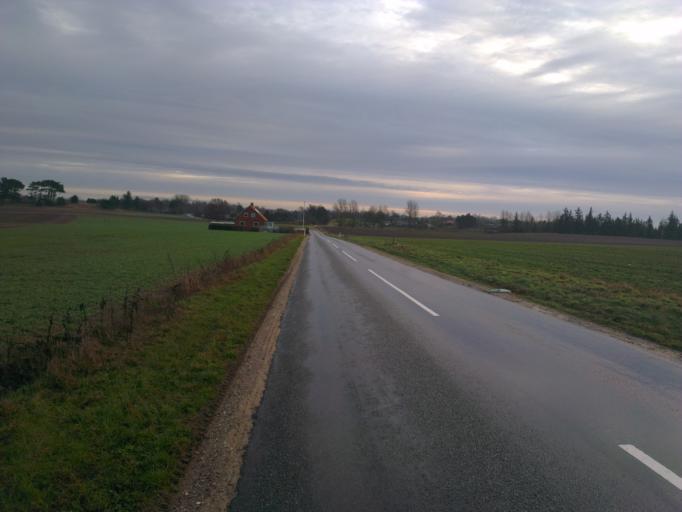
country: DK
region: Capital Region
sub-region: Frederikssund Kommune
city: Jaegerspris
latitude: 55.8261
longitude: 11.9776
